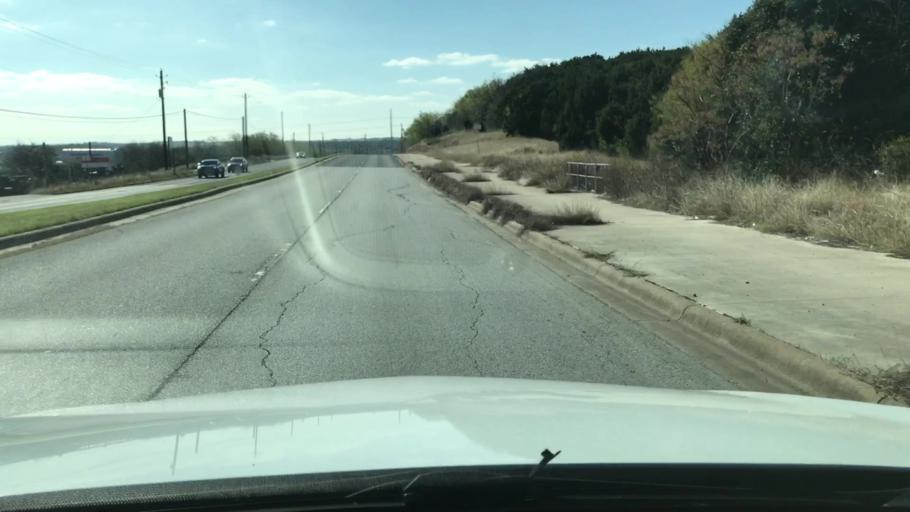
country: US
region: Texas
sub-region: Travis County
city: Onion Creek
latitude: 30.1707
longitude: -97.7225
